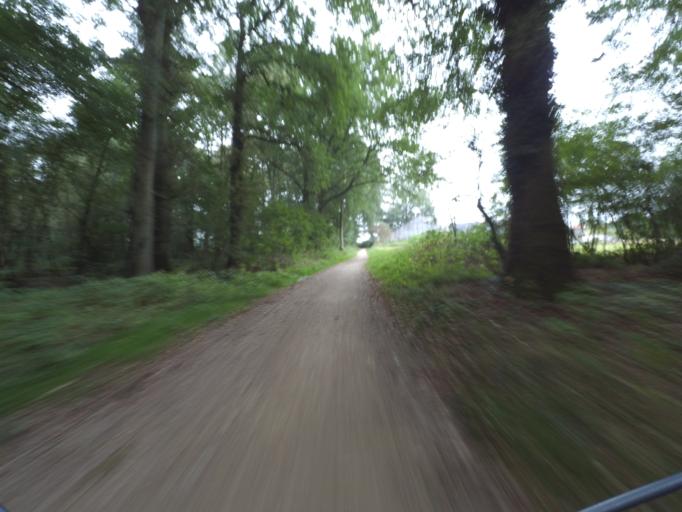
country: DE
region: Lower Saxony
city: Nordhorn
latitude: 52.3417
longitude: 7.0570
